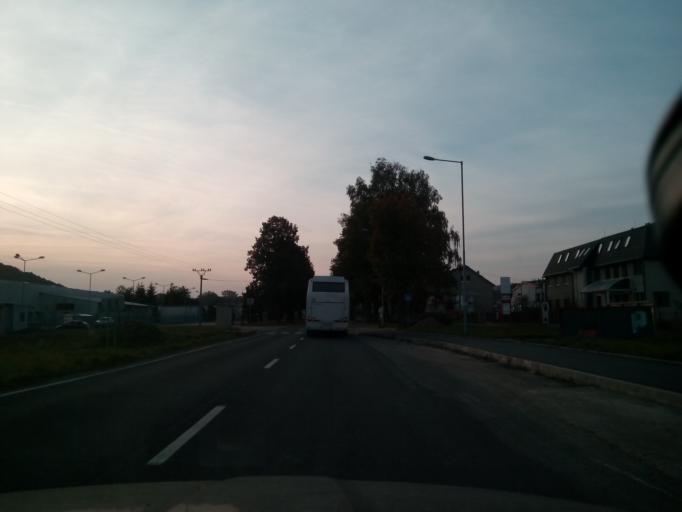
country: SK
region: Presovsky
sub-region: Okres Bardejov
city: Bardejov
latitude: 49.3035
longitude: 21.3061
